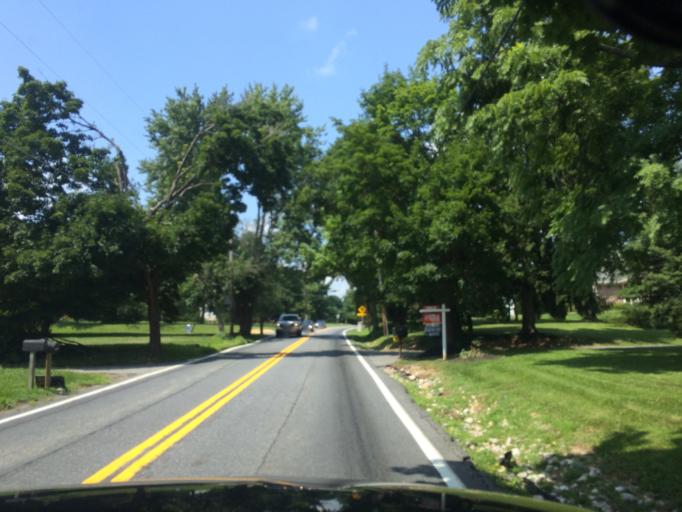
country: US
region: Maryland
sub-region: Carroll County
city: Sykesville
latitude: 39.4056
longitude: -77.0168
